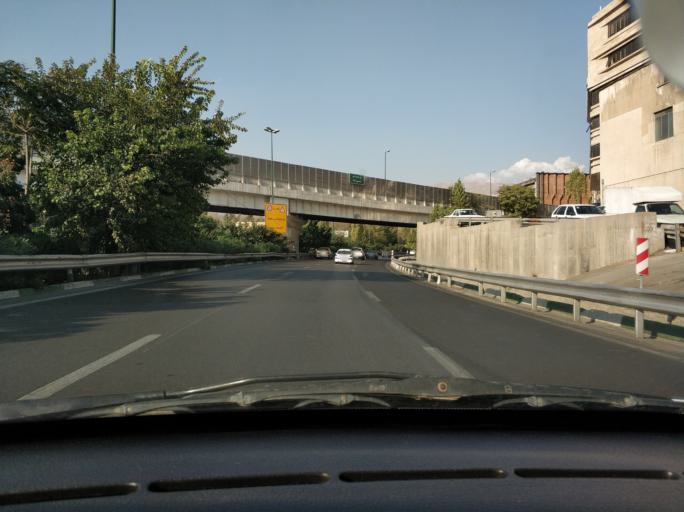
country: IR
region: Tehran
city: Tajrish
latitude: 35.7782
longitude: 51.4774
